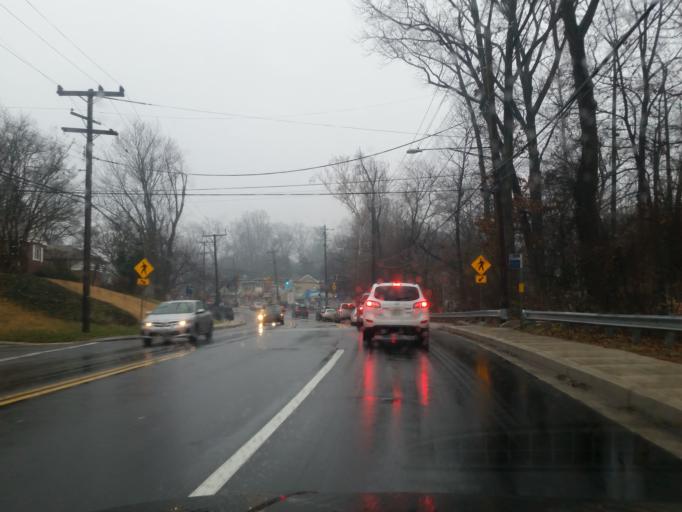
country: US
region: Maryland
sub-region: Montgomery County
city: Takoma Park
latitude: 38.9947
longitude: -77.0081
